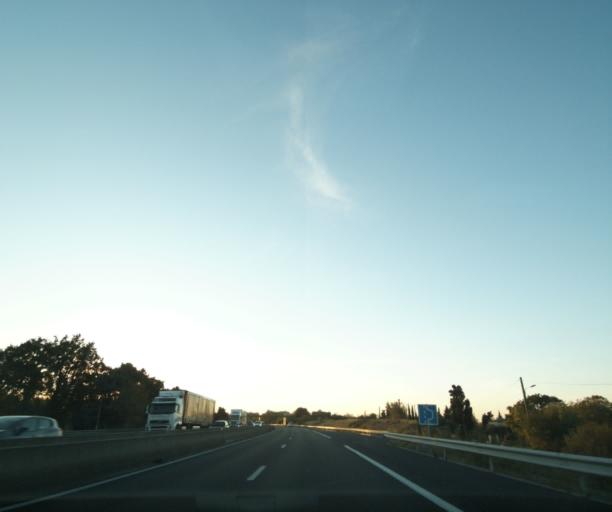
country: FR
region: Provence-Alpes-Cote d'Azur
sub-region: Departement des Bouches-du-Rhone
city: Salon-de-Provence
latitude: 43.6261
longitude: 5.0906
